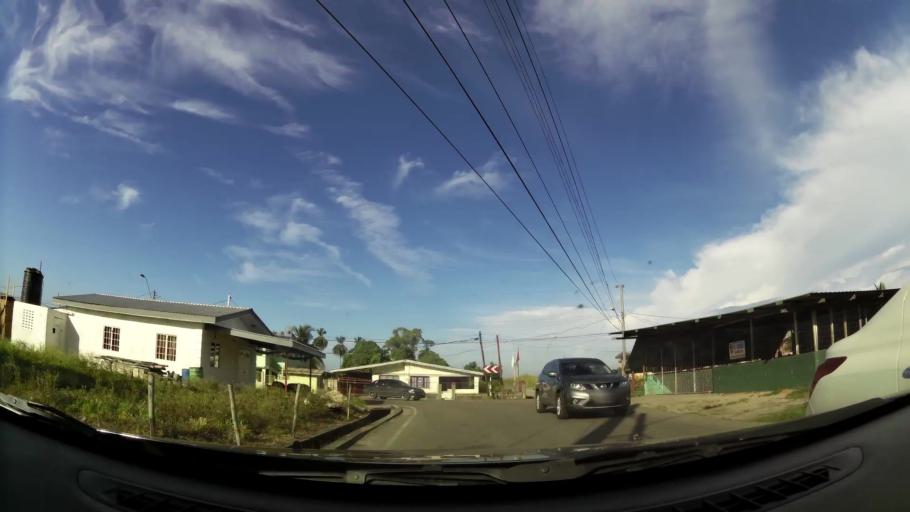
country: TT
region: Tunapuna/Piarco
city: Tunapuna
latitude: 10.5777
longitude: -61.3808
